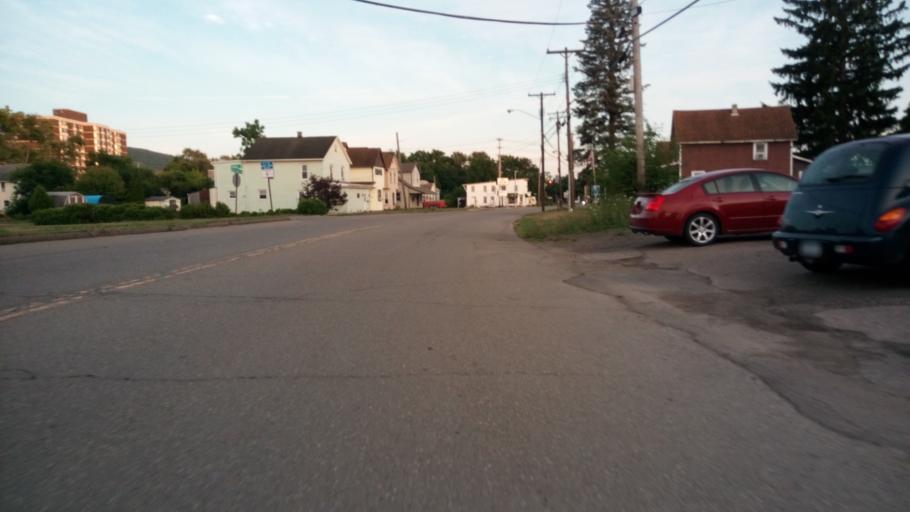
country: US
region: New York
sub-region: Chemung County
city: Elmira Heights
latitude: 42.1313
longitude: -76.8188
